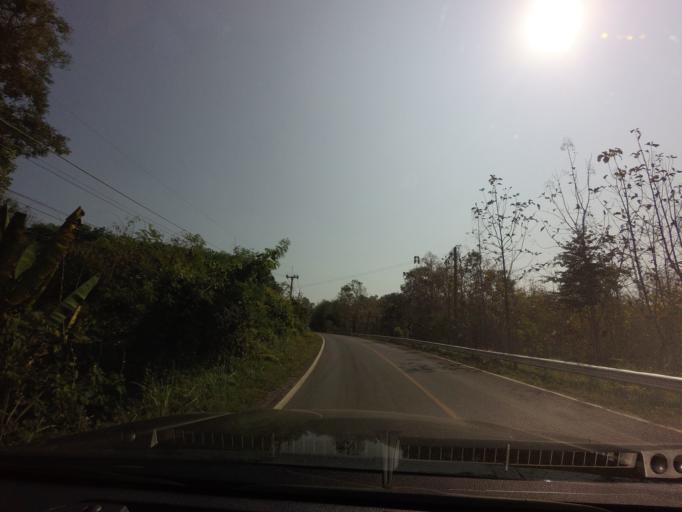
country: TH
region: Kanchanaburi
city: Thong Pha Phum
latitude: 14.6535
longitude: 98.5530
